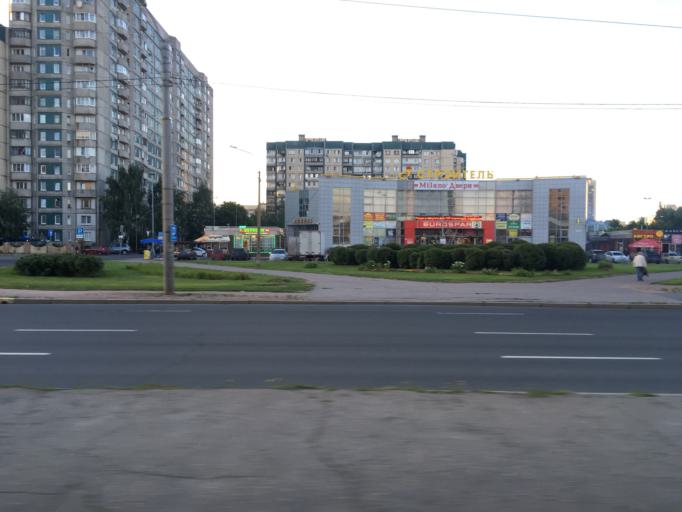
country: RU
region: St.-Petersburg
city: Komendantsky aerodrom
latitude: 60.0065
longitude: 30.2713
